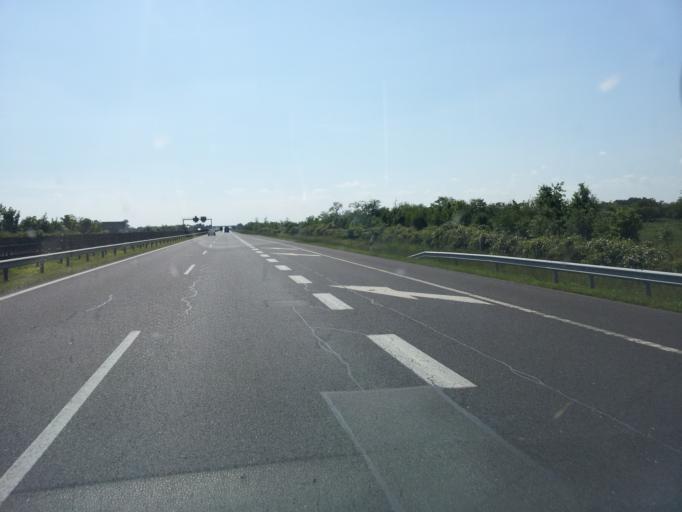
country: HU
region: Borsod-Abauj-Zemplen
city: Emod
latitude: 47.8741
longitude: 20.8068
